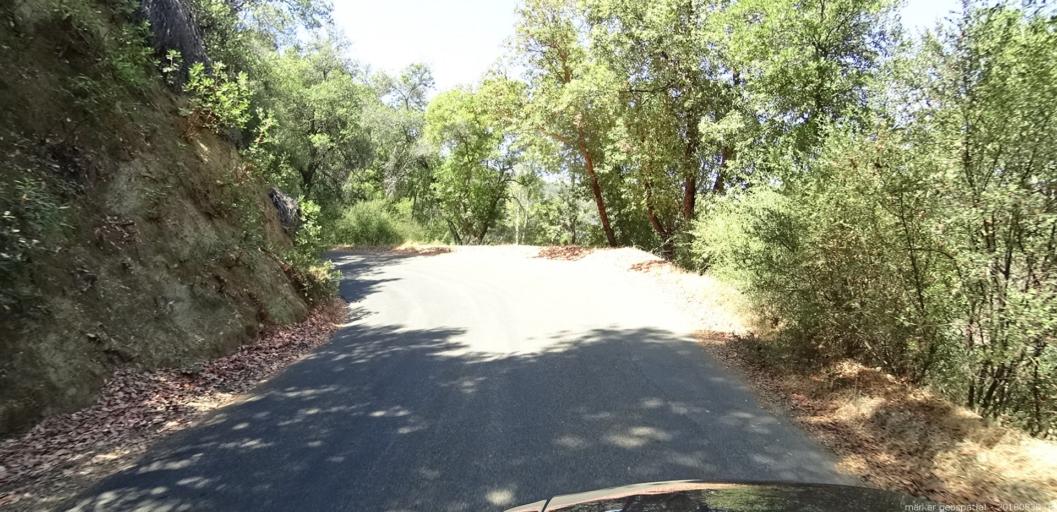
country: US
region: California
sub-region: Monterey County
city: Greenfield
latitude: 36.0134
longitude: -121.4387
